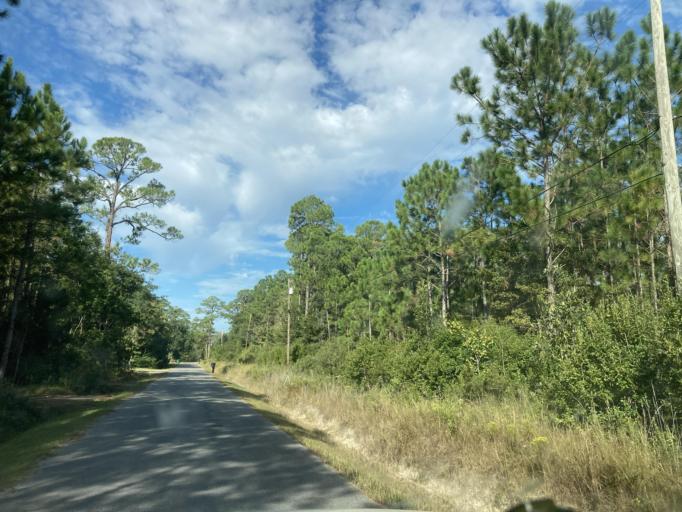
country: US
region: Mississippi
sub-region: Jackson County
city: Saint Martin
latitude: 30.4385
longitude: -88.8670
